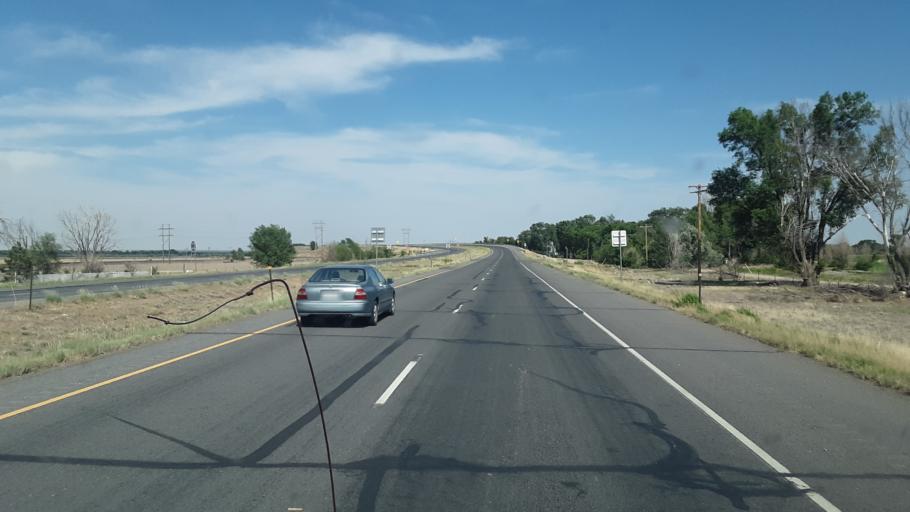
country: US
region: Colorado
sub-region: Otero County
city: Rocky Ford
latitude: 38.1029
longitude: -103.8503
